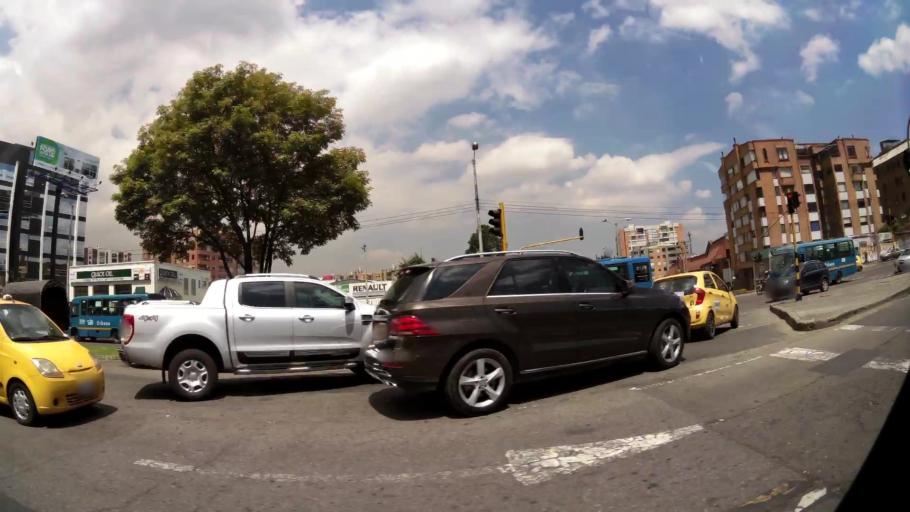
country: CO
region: Bogota D.C.
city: Barrio San Luis
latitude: 4.7227
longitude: -74.0261
